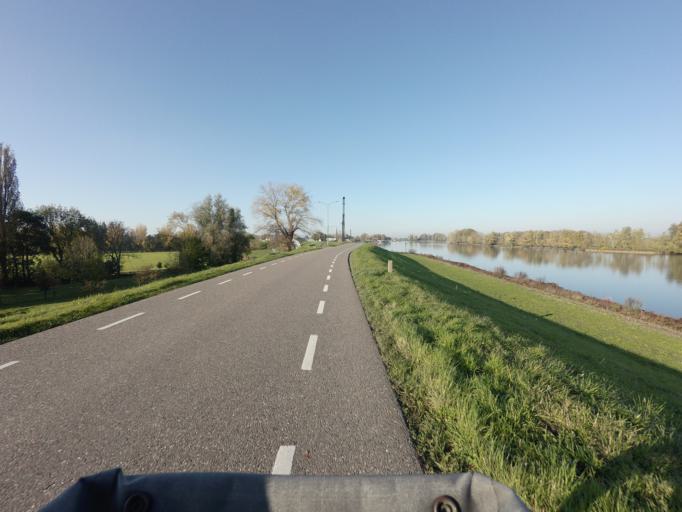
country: NL
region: North Brabant
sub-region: Gemeente Woudrichem
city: Woudrichem
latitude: 51.8091
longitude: 5.0122
